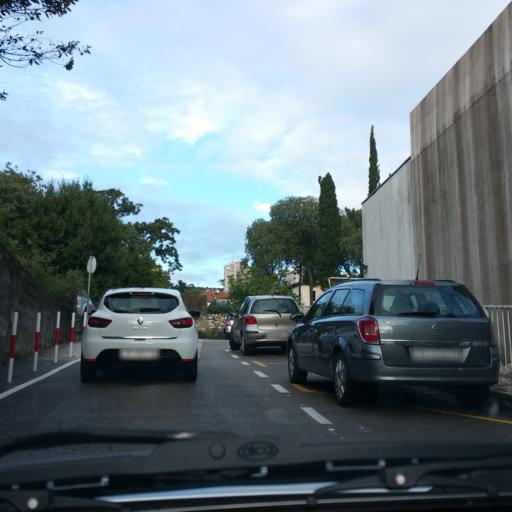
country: HR
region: Primorsko-Goranska
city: Drenova
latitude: 45.3329
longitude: 14.4256
